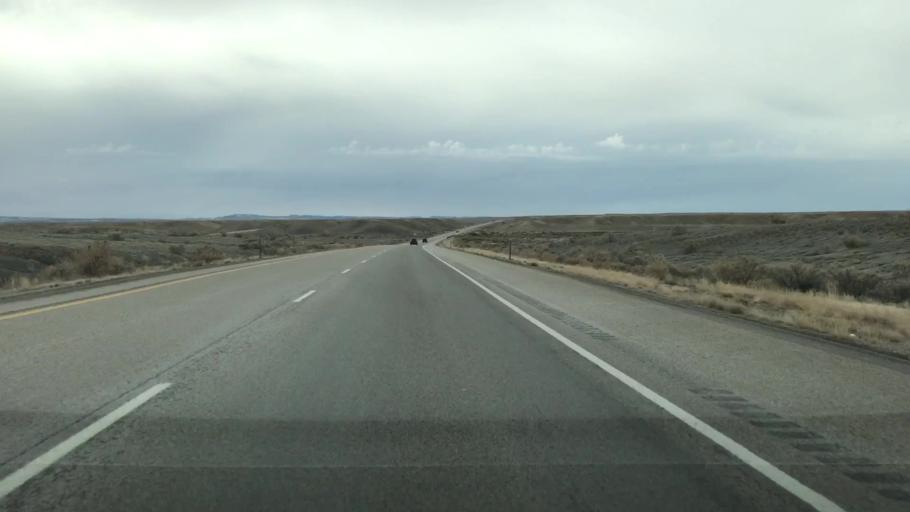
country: US
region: Utah
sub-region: Grand County
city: Moab
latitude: 38.9807
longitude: -109.3472
